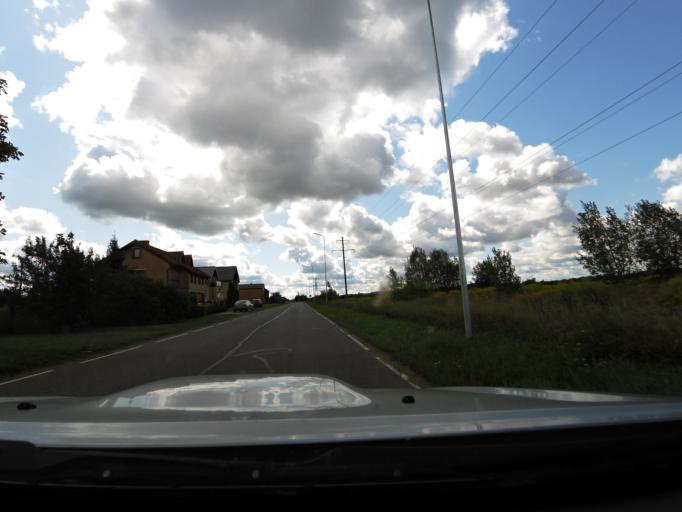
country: LV
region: Daugavpils
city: Daugavpils
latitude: 55.8675
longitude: 26.4922
